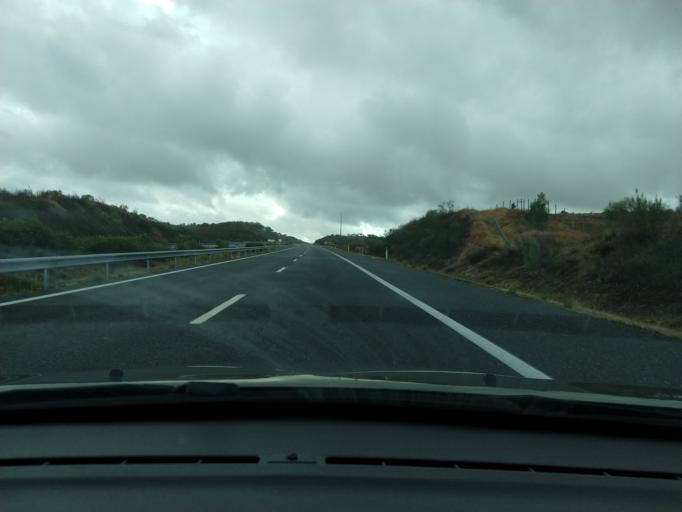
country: PT
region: Beja
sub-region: Almodovar
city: Almodovar
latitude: 37.4876
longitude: -8.2085
